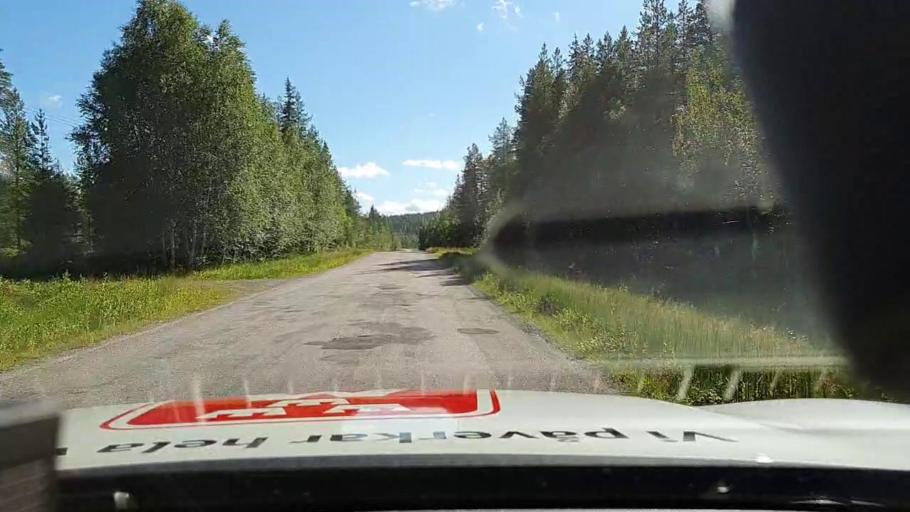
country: SE
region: Norrbotten
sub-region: Overkalix Kommun
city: OEverkalix
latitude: 66.2500
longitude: 23.0105
